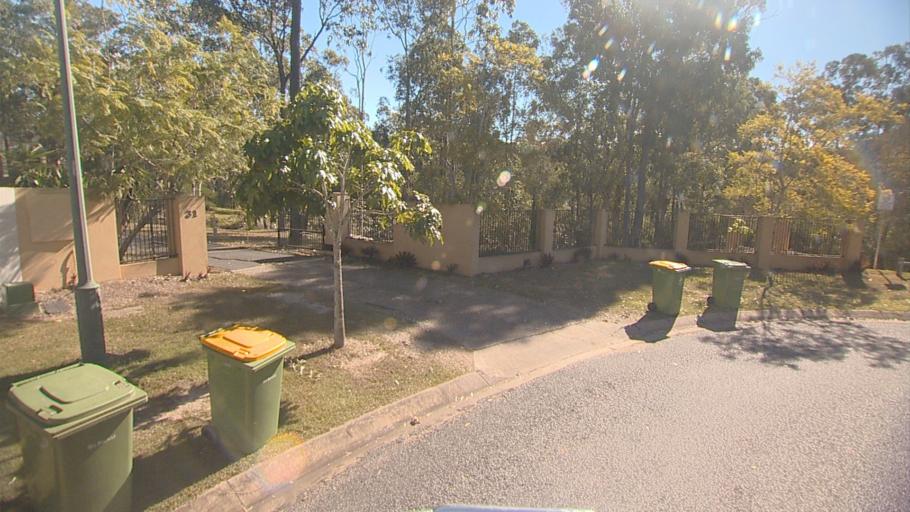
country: AU
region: Queensland
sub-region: Ipswich
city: Springfield Lakes
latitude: -27.7308
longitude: 152.9113
